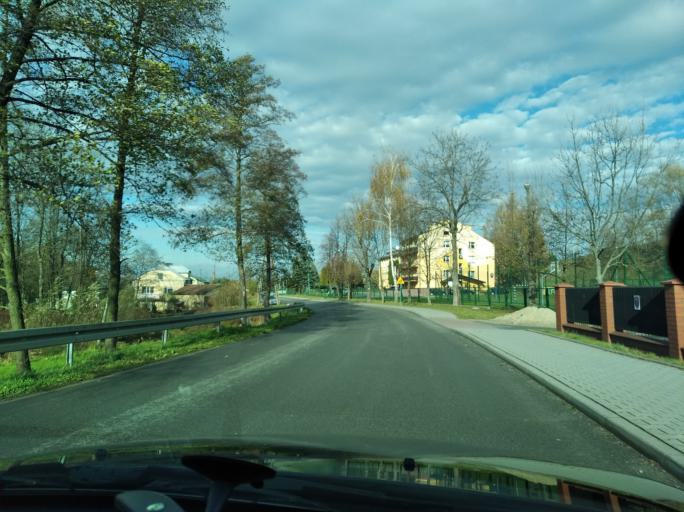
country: PL
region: Subcarpathian Voivodeship
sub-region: Powiat debicki
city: Brzeznica
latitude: 50.0501
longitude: 21.4866
